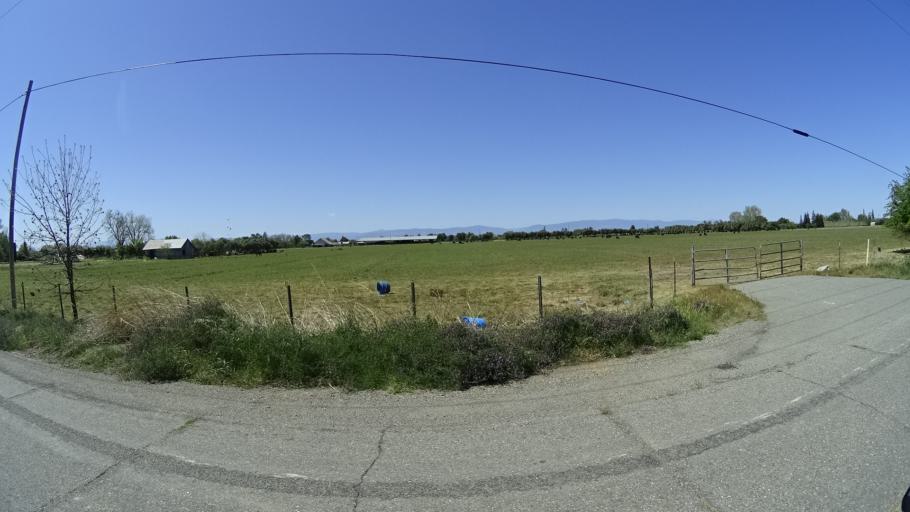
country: US
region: California
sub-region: Glenn County
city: Orland
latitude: 39.7854
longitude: -122.2065
